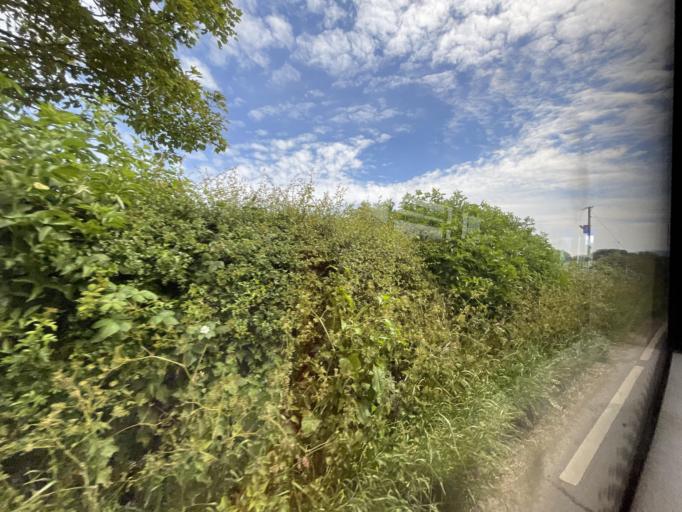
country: GB
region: Wales
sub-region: Anglesey
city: Beaumaris
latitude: 53.2758
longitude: -4.1196
